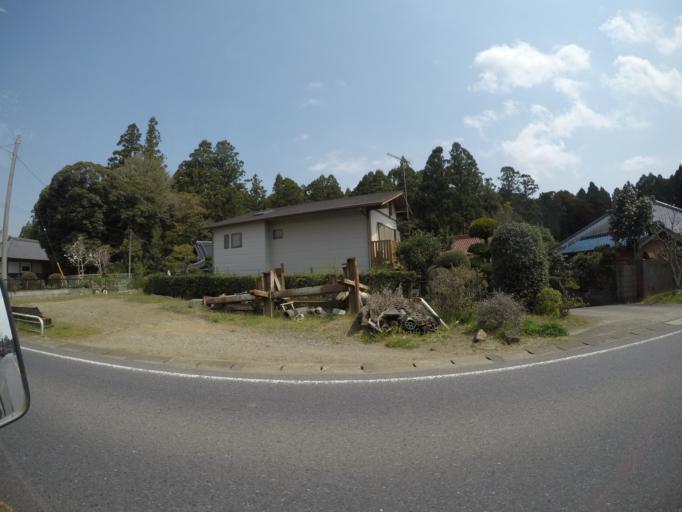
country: JP
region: Chiba
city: Sawara
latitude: 35.8704
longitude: 140.5388
